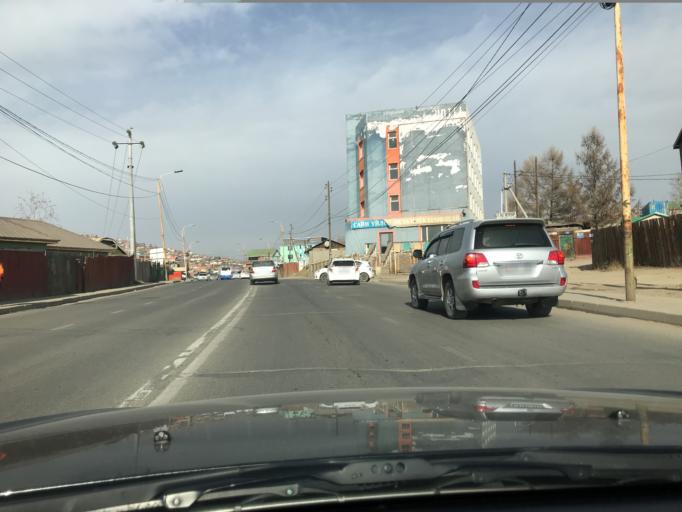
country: MN
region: Ulaanbaatar
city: Ulaanbaatar
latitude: 47.9336
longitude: 106.8866
